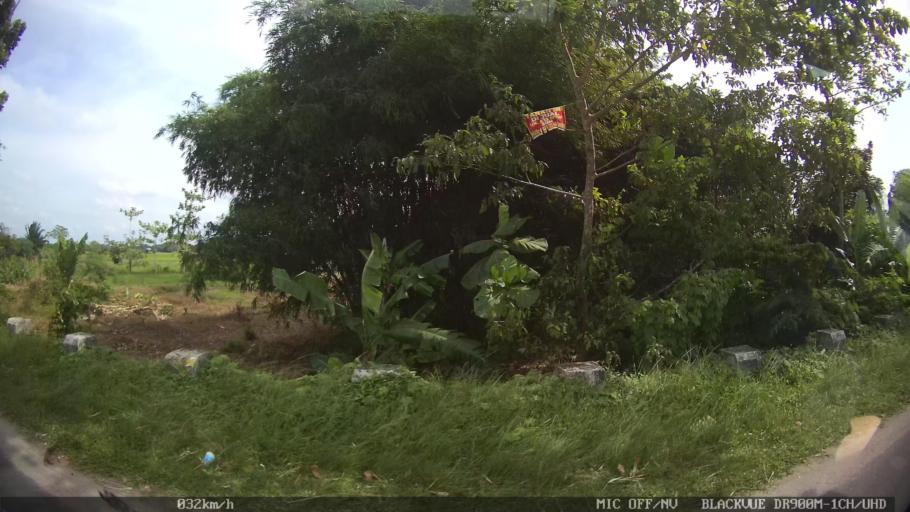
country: ID
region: North Sumatra
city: Percut
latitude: 3.6156
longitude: 98.8381
